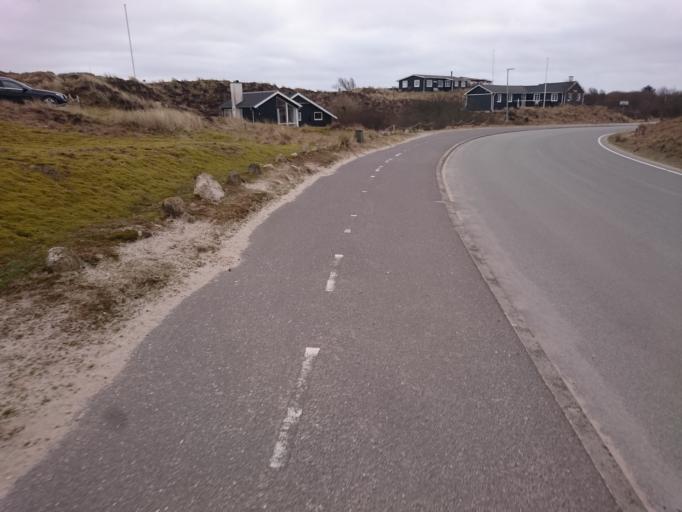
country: DK
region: South Denmark
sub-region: Fano Kommune
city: Nordby
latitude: 55.4235
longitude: 8.3869
